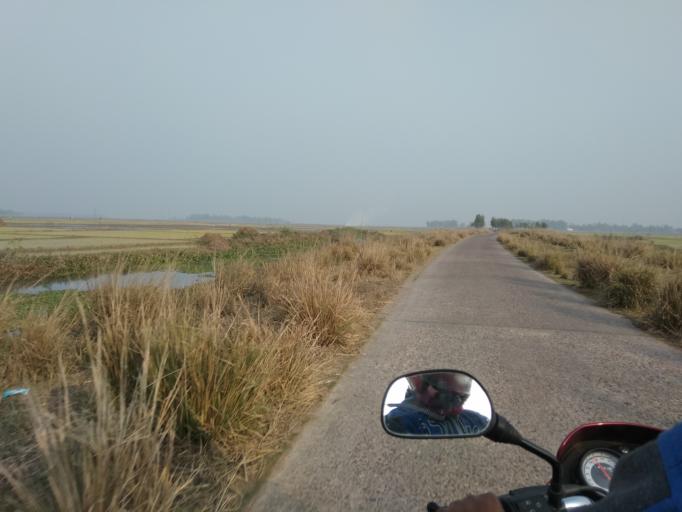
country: BD
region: Rajshahi
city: Ishurdi
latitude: 24.4962
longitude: 89.1876
